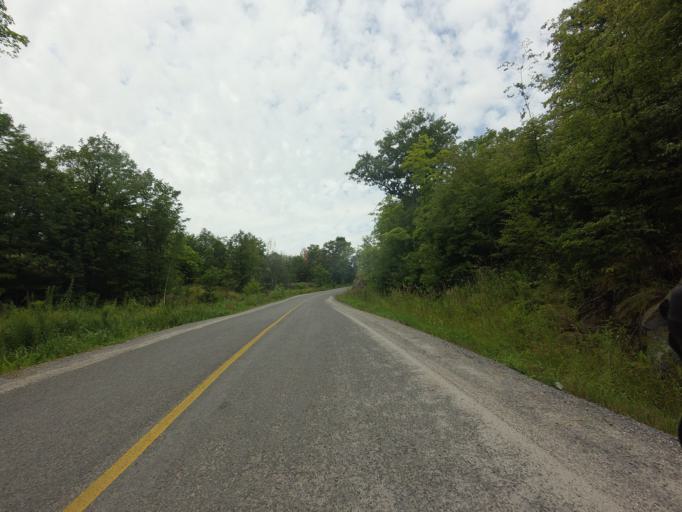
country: CA
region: Ontario
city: Perth
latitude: 44.6747
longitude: -76.6602
